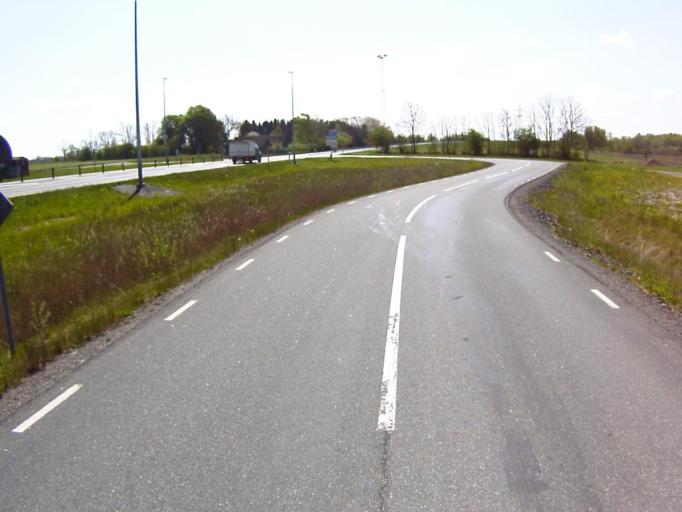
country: SE
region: Skane
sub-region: Kristianstads Kommun
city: Fjalkinge
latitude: 56.0014
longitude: 14.2661
